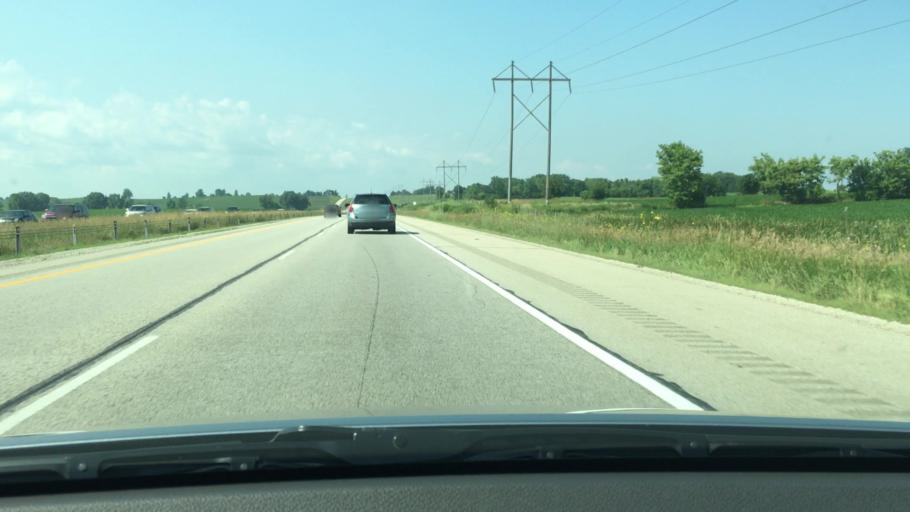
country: US
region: Wisconsin
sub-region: Fond du Lac County
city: Rosendale
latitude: 43.8779
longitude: -88.5839
